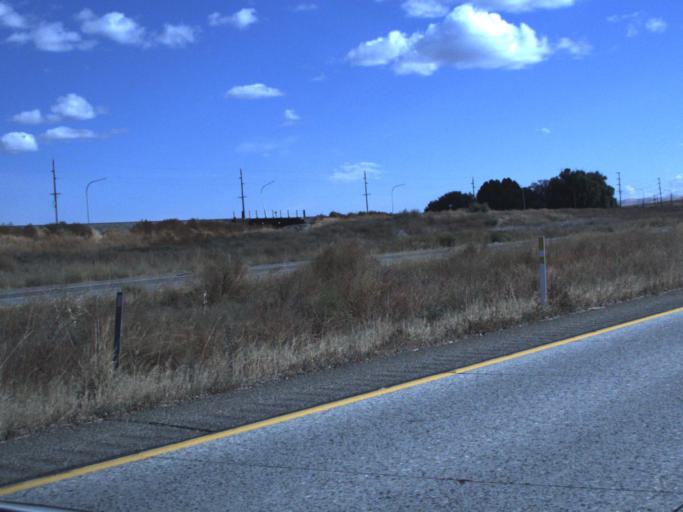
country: US
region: Washington
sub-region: Yakima County
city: Grandview
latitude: 46.2762
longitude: -119.9327
